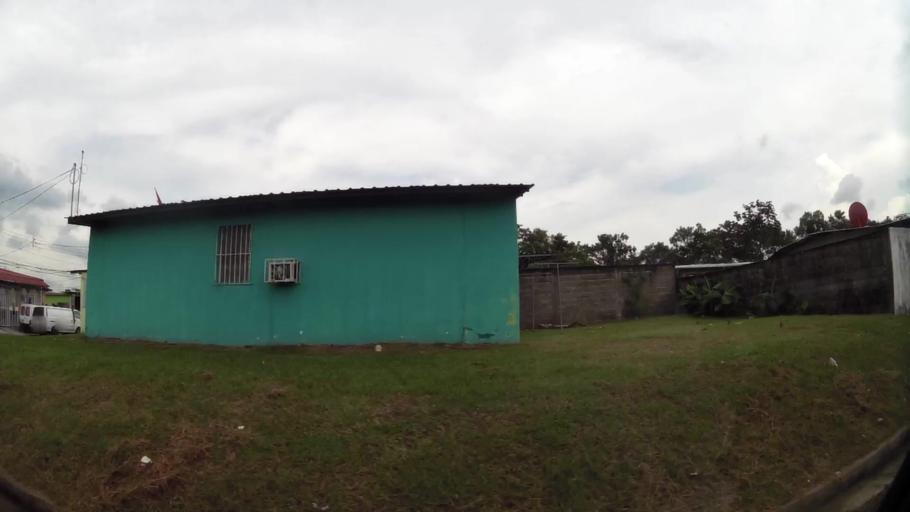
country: PA
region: Panama
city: Cabra Numero Uno
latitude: 9.0973
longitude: -79.3441
